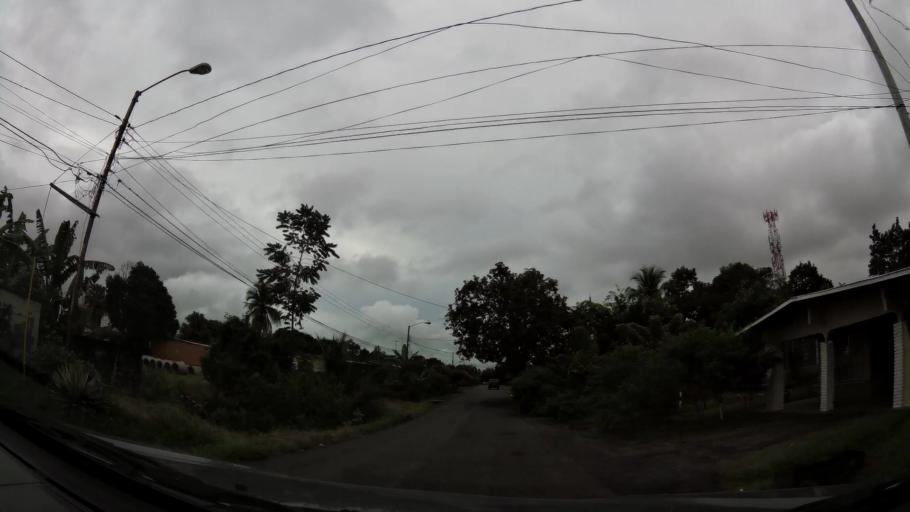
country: PA
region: Chiriqui
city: David
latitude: 8.4268
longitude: -82.4397
